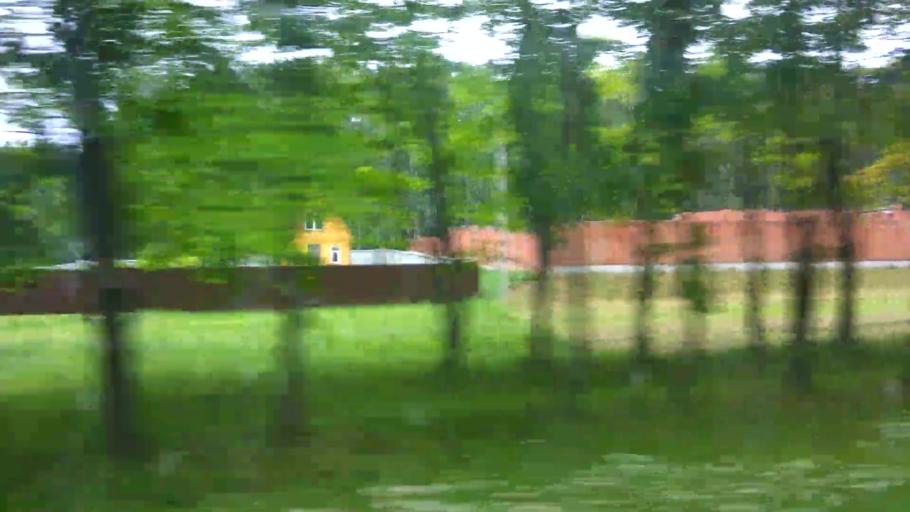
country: RU
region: Moskovskaya
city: Ozherel'ye
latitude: 54.8330
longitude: 38.2812
